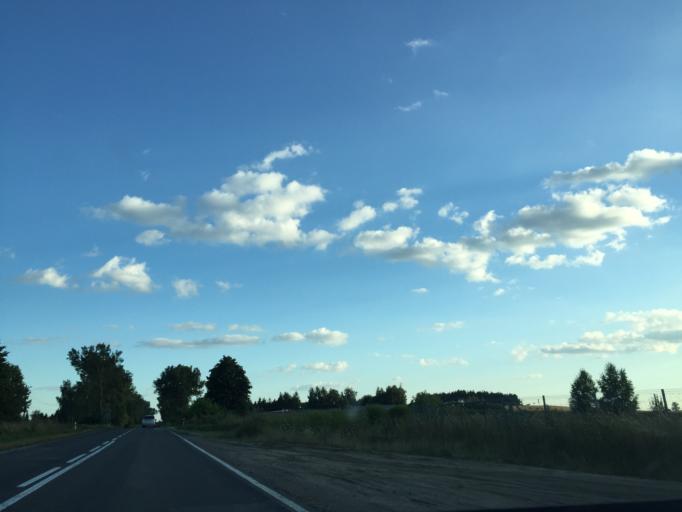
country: PL
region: Podlasie
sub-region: Lomza
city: Lomza
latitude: 53.1126
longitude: 22.0299
